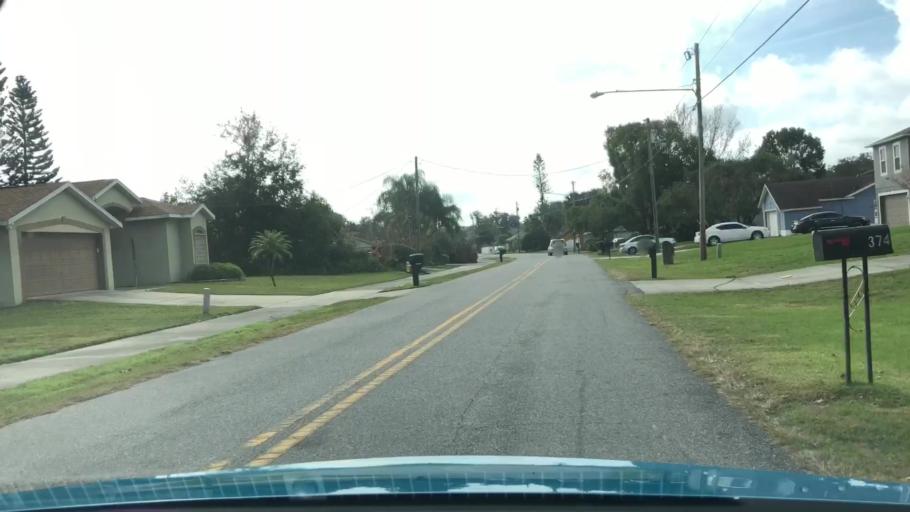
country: US
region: Florida
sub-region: Volusia County
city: Deltona
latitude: 28.8720
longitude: -81.2465
